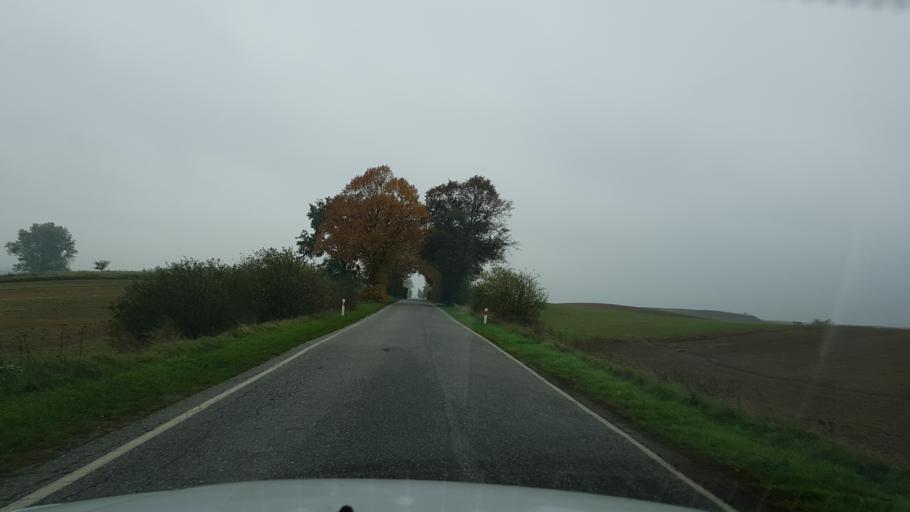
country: PL
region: West Pomeranian Voivodeship
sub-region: Powiat stargardzki
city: Dolice
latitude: 53.1803
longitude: 15.2112
